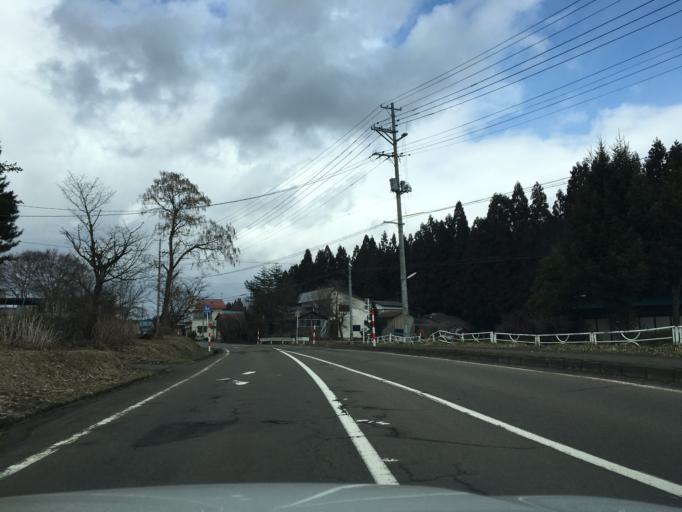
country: JP
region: Akita
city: Takanosu
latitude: 40.1549
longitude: 140.3355
